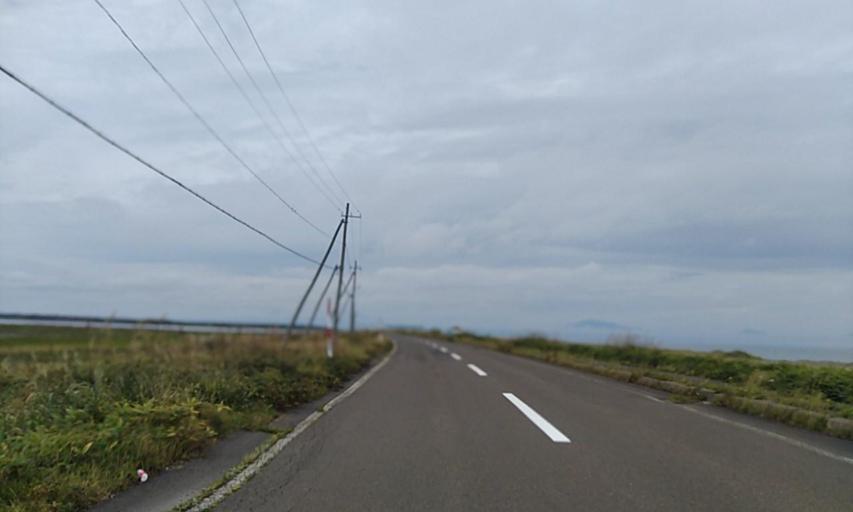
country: JP
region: Hokkaido
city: Shibetsu
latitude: 43.5968
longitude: 145.3222
